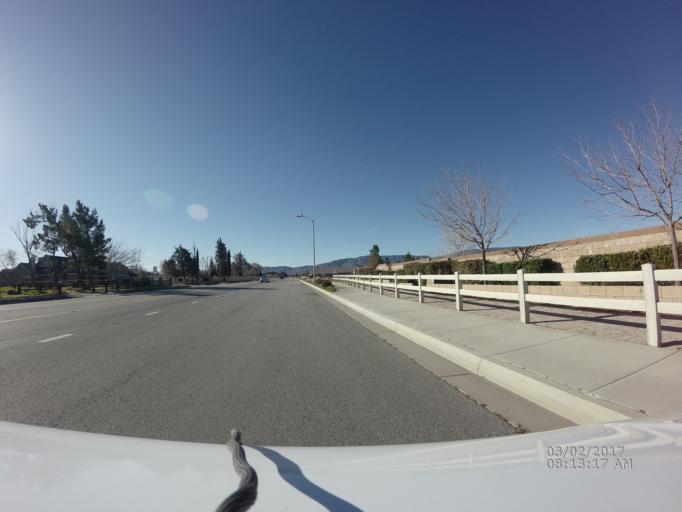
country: US
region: California
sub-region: Los Angeles County
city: Quartz Hill
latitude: 34.6411
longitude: -118.1833
